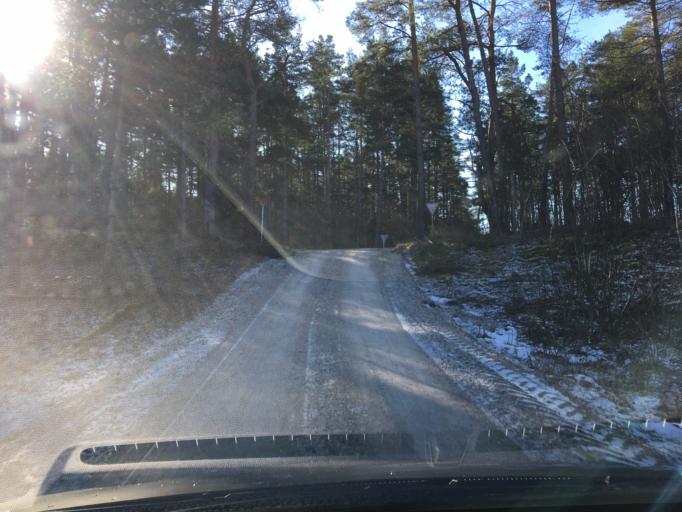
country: EE
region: Laeaene
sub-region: Lihula vald
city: Lihula
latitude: 58.5677
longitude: 23.6917
